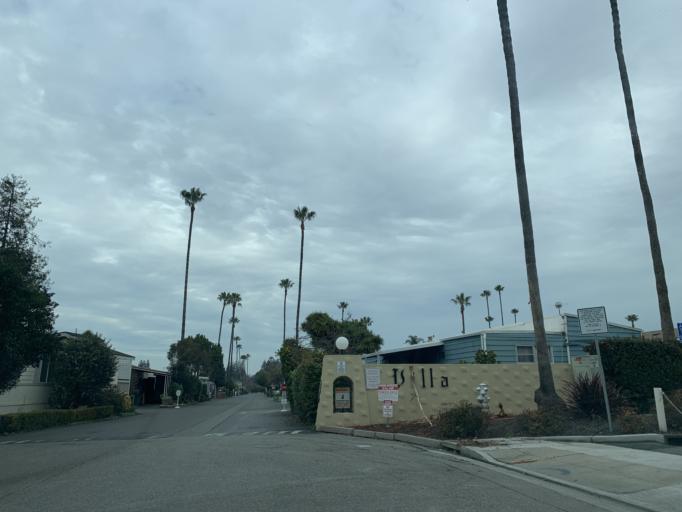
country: US
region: California
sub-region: Santa Clara County
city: Mountain View
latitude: 37.4140
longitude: -122.0724
